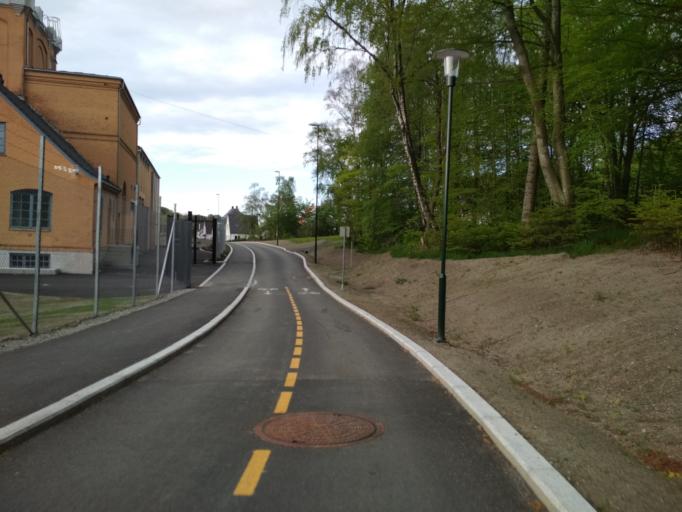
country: NO
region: Rogaland
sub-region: Stavanger
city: Stavanger
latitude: 58.9576
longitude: 5.7239
